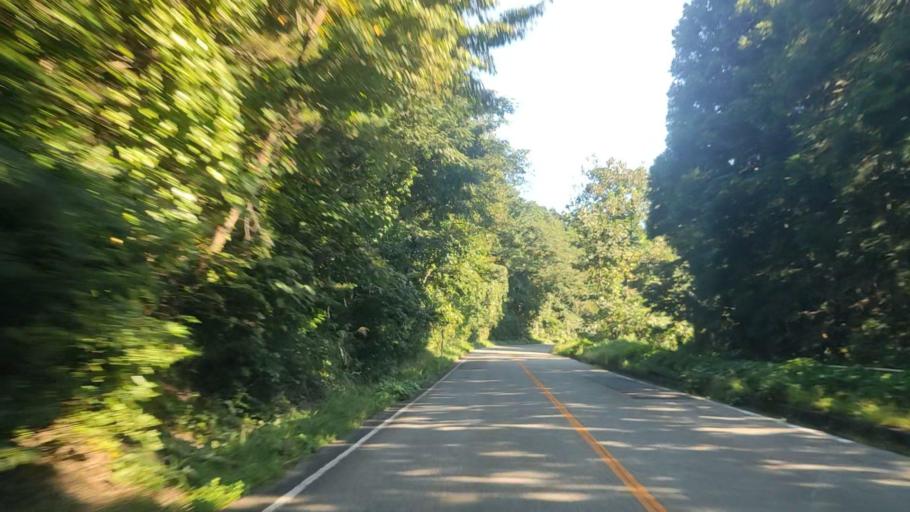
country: JP
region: Ishikawa
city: Nanao
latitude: 37.1065
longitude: 136.9467
